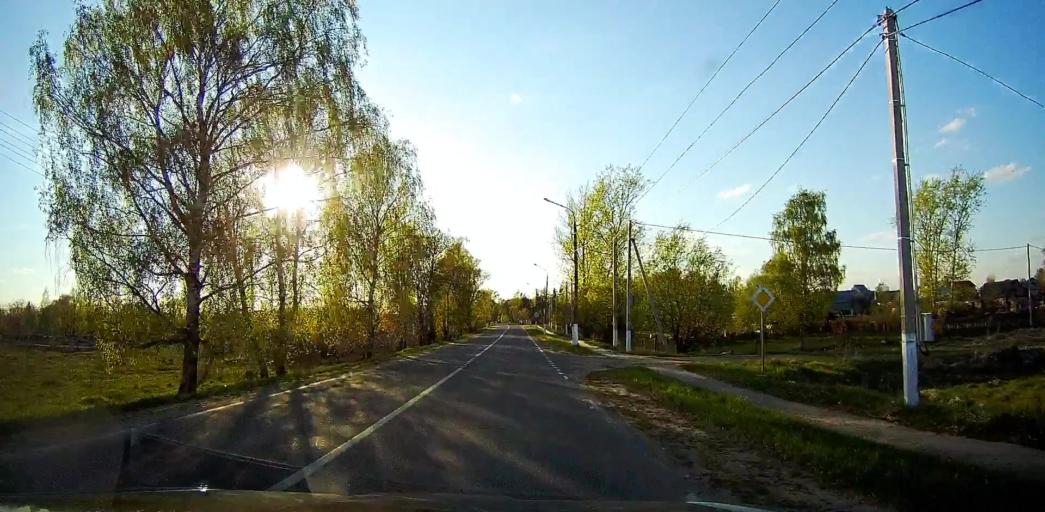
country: RU
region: Moskovskaya
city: Malino
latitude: 55.2782
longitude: 38.1631
